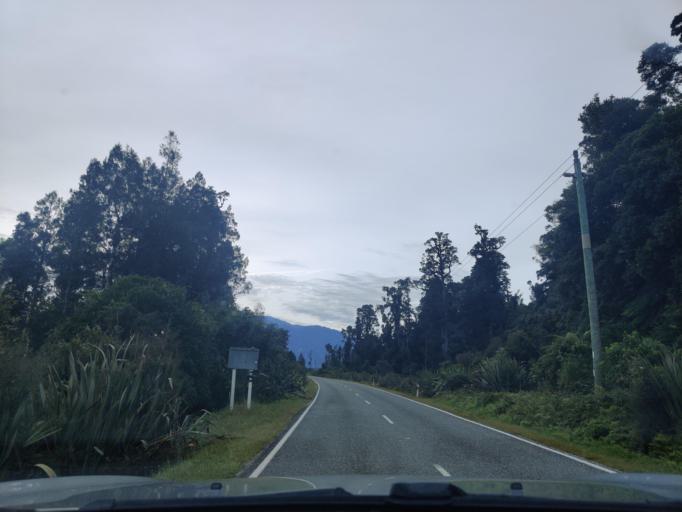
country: NZ
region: West Coast
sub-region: Westland District
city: Hokitika
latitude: -43.2554
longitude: 170.2713
